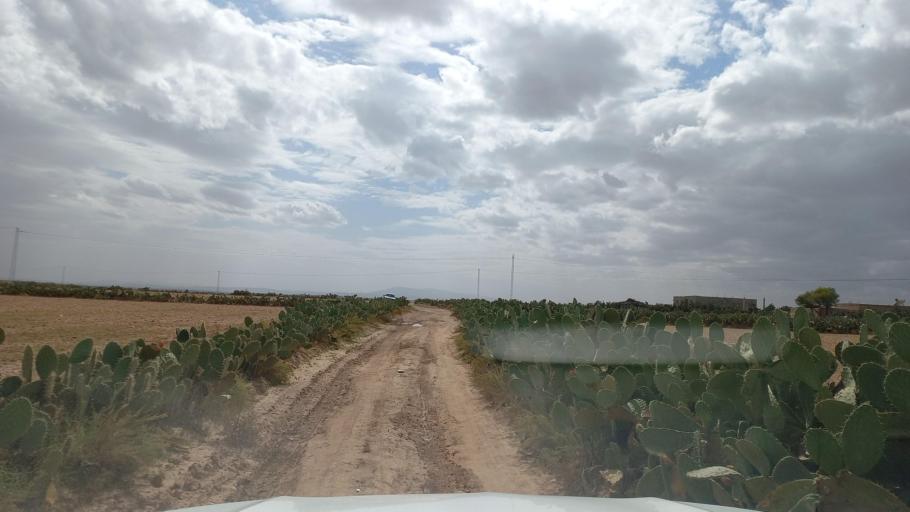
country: TN
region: Al Qasrayn
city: Sbiba
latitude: 35.3823
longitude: 9.0946
